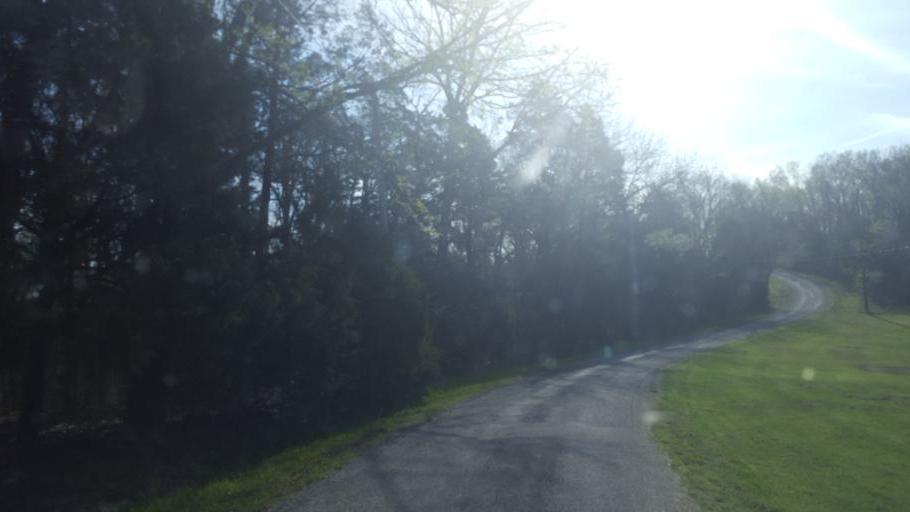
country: US
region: Kentucky
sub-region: Edmonson County
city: Brownsville
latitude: 37.3282
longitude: -86.1067
